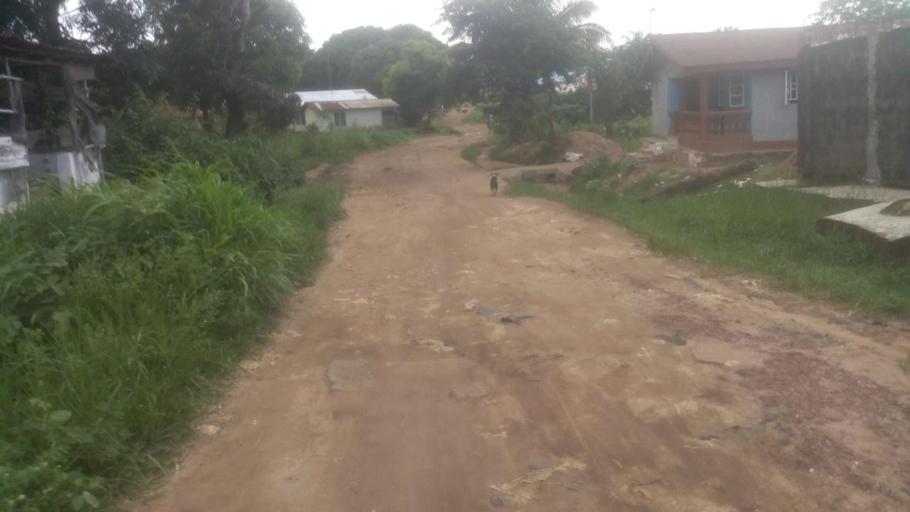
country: SL
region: Northern Province
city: Masoyila
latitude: 8.6085
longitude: -13.1920
